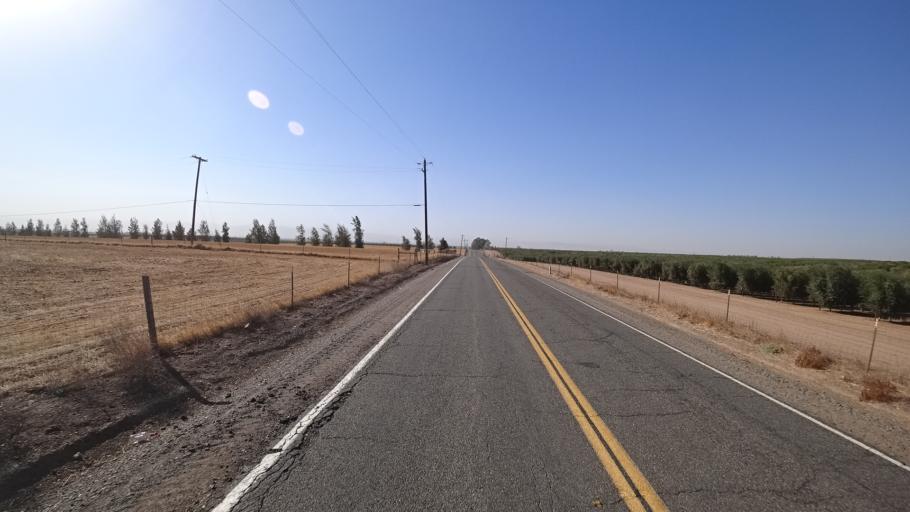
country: US
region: California
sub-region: Yolo County
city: Cottonwood
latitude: 38.7117
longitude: -121.9030
